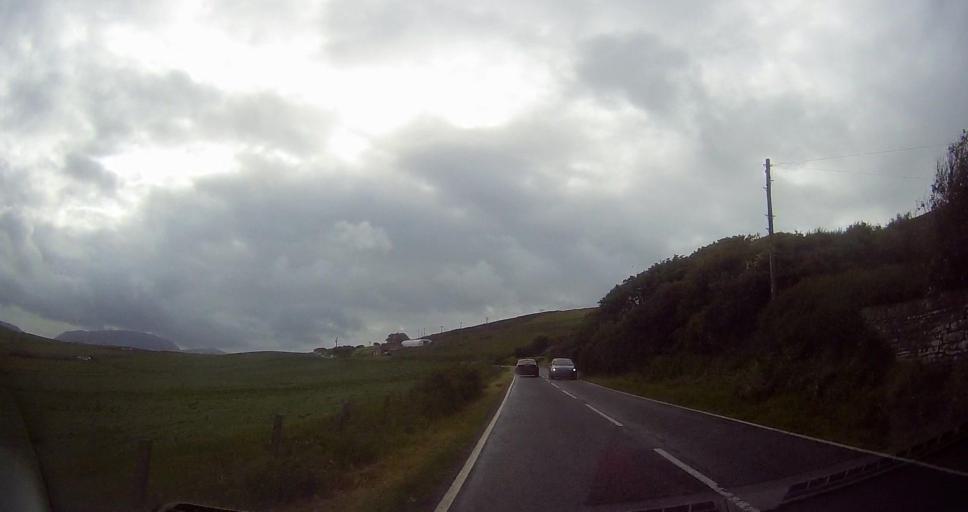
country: GB
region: Scotland
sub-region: Orkney Islands
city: Stromness
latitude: 58.9204
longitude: -3.1843
